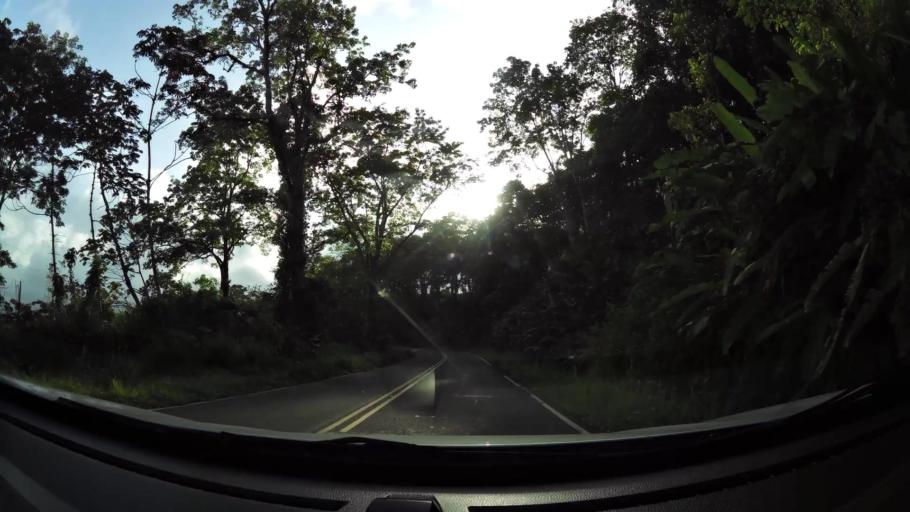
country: CR
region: Limon
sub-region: Canton de Siquirres
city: Siquirres
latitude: 10.0241
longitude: -83.5595
